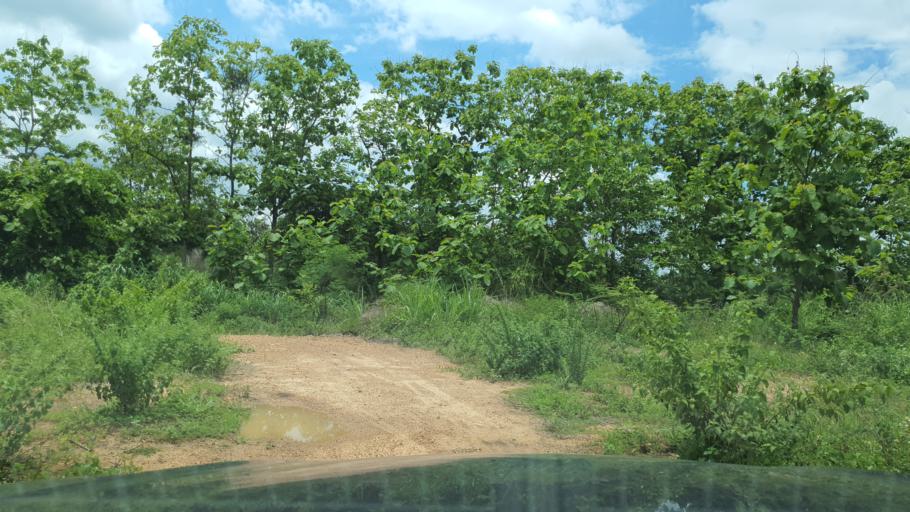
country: TH
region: Chiang Mai
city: San Sai
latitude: 18.9239
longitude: 99.0558
